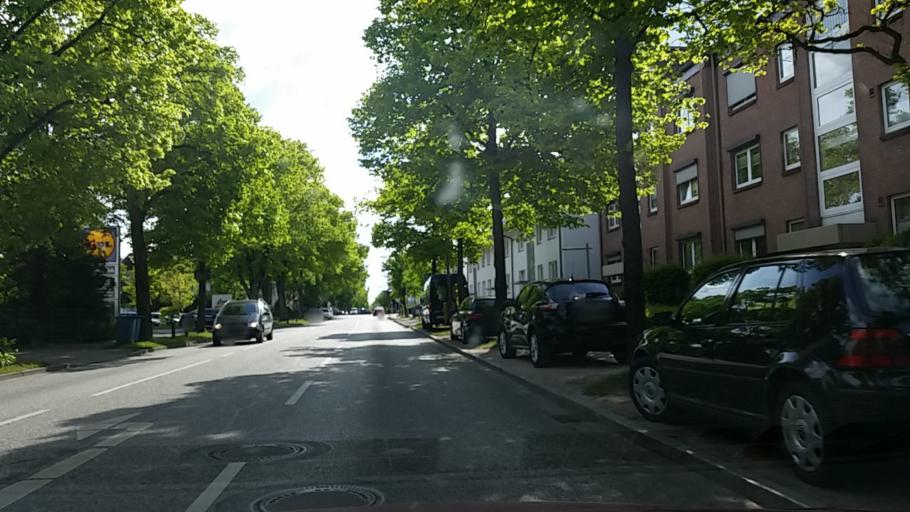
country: DE
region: Schleswig-Holstein
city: Ahrensburg
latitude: 53.6688
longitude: 10.2306
